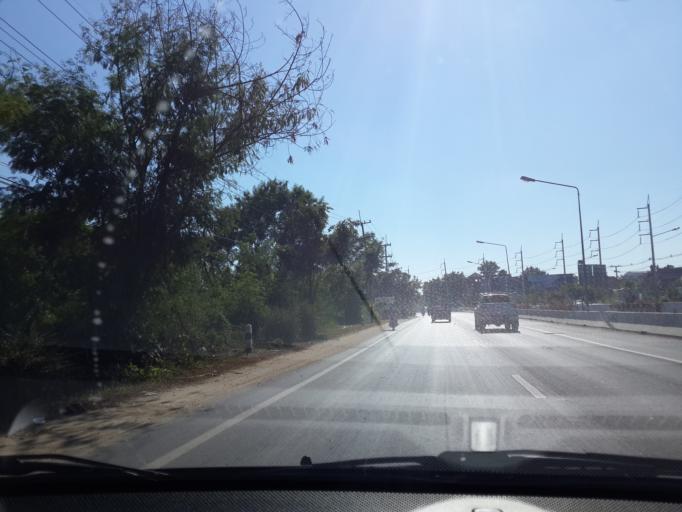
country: TH
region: Chiang Mai
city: Chiang Mai
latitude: 18.7609
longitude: 98.9444
